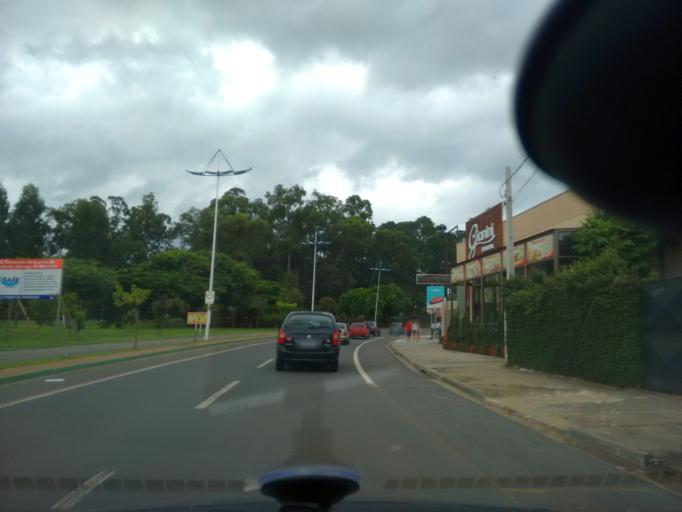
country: BR
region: Sao Paulo
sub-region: Indaiatuba
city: Indaiatuba
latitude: -23.0805
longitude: -47.2228
